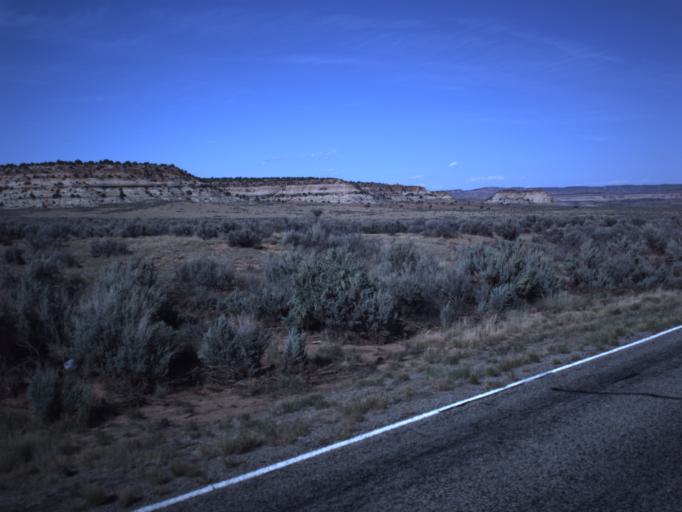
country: US
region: Utah
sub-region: San Juan County
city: Monticello
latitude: 38.0622
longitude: -109.3951
